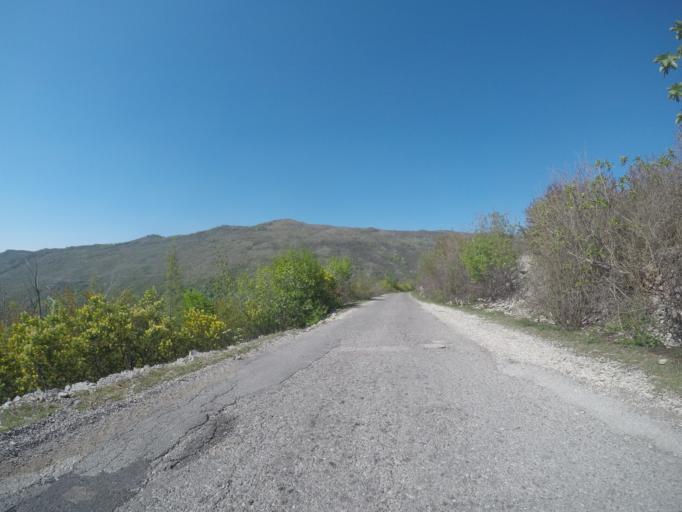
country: ME
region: Danilovgrad
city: Danilovgrad
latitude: 42.5147
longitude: 19.0747
